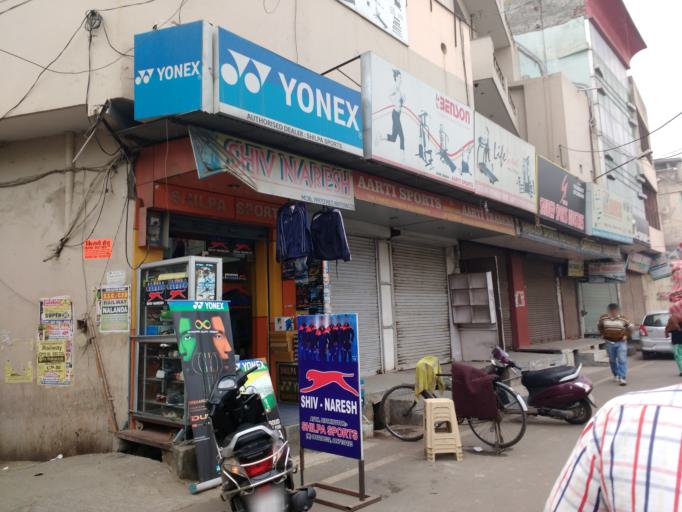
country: IN
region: Uttar Pradesh
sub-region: Meerut
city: Meerut
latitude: 28.9764
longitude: 77.7164
